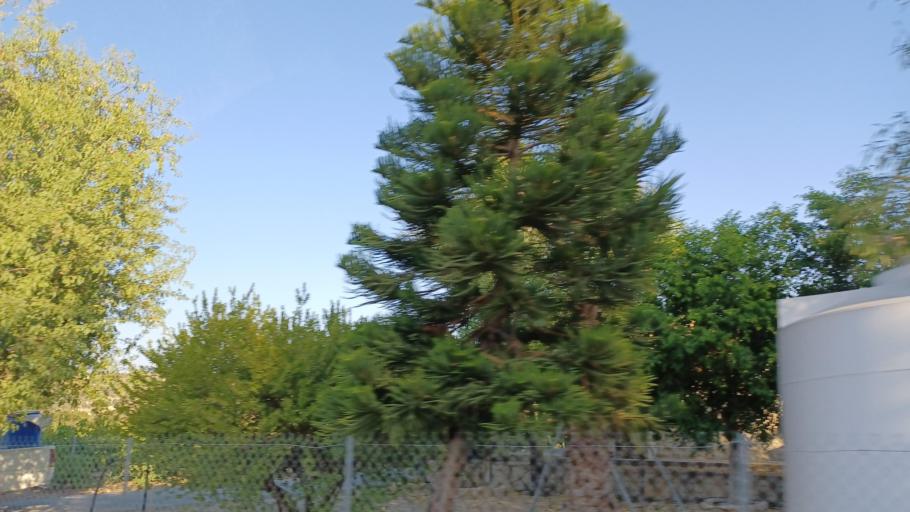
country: CY
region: Limassol
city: Pissouri
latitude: 34.7057
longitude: 32.6782
